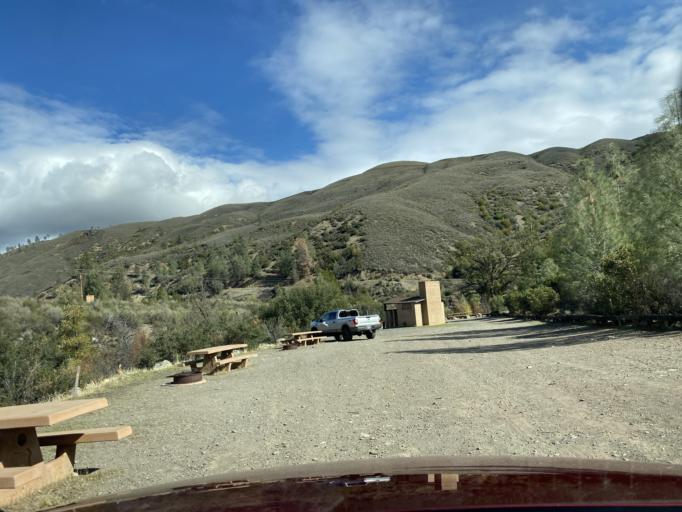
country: US
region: California
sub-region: Lake County
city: Lucerne
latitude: 39.3556
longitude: -122.6553
